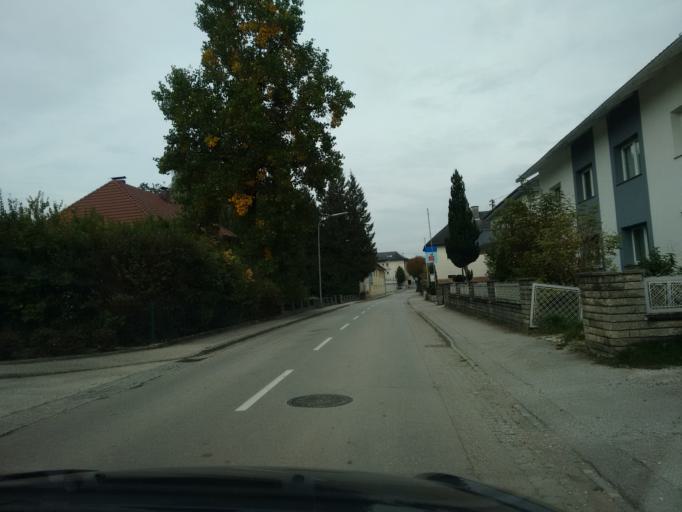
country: AT
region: Upper Austria
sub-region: Politischer Bezirk Grieskirchen
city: Bad Schallerbach
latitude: 48.1834
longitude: 13.8977
